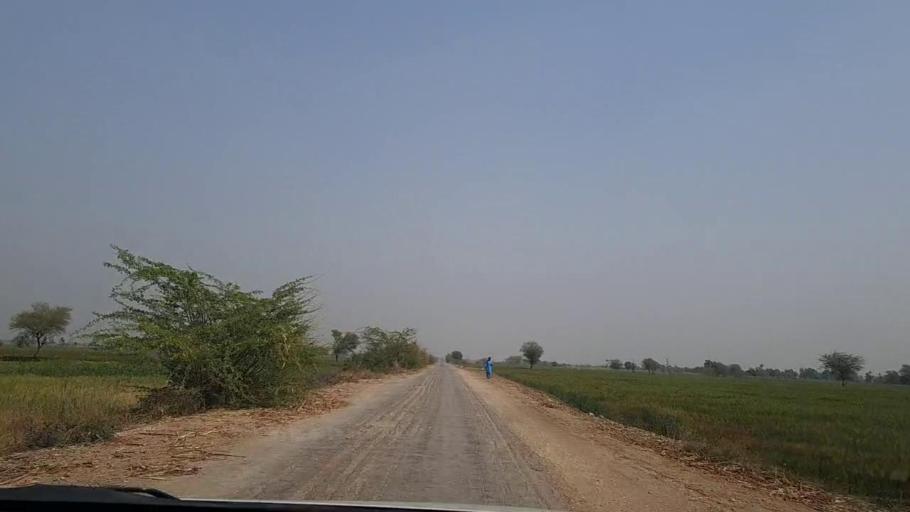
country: PK
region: Sindh
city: Pithoro
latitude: 25.5679
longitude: 69.2398
